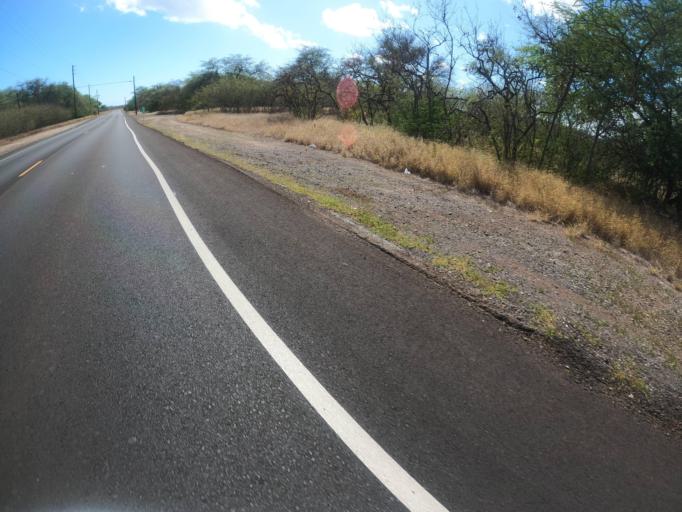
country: US
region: Hawaii
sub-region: Honolulu County
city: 'Ewa Villages
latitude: 21.3222
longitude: -158.0560
